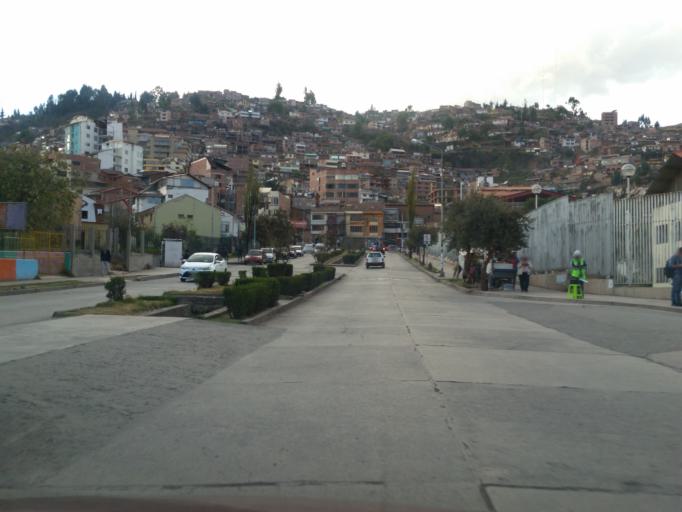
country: PE
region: Cusco
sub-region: Provincia de Cusco
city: Cusco
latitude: -13.5211
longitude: -71.9609
